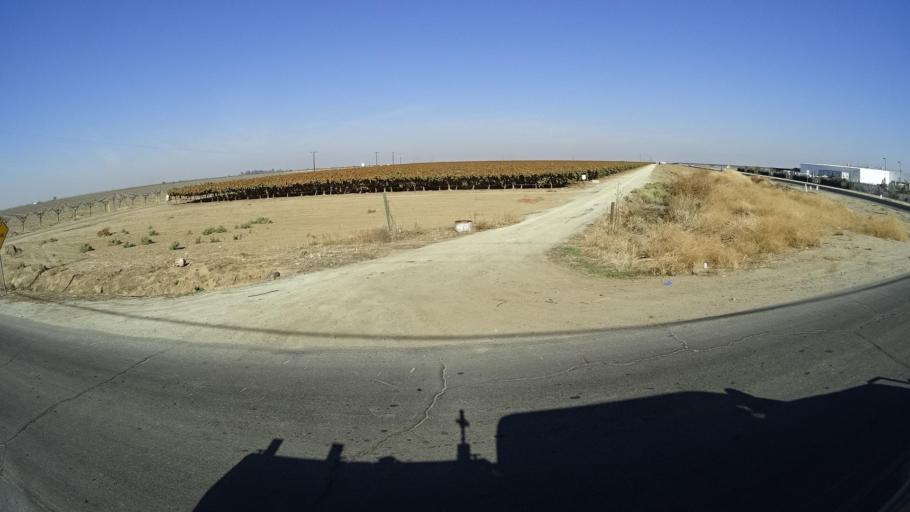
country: US
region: California
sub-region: Kern County
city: McFarland
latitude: 35.7180
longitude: -119.1601
